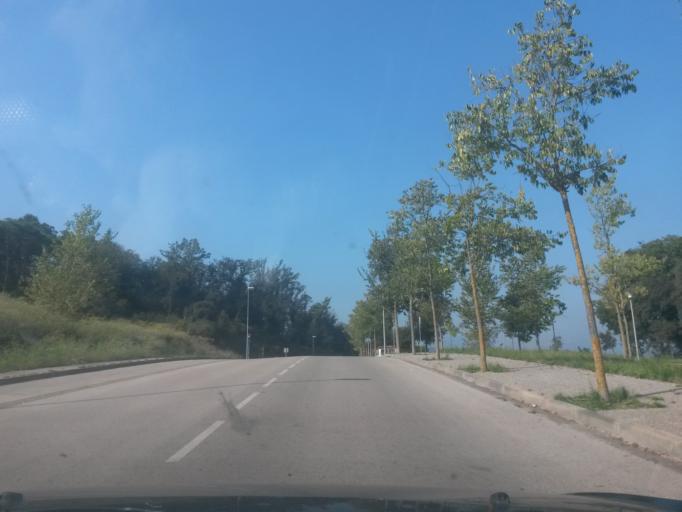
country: ES
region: Catalonia
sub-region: Provincia de Girona
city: Fornells de la Selva
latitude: 41.9537
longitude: 2.8122
